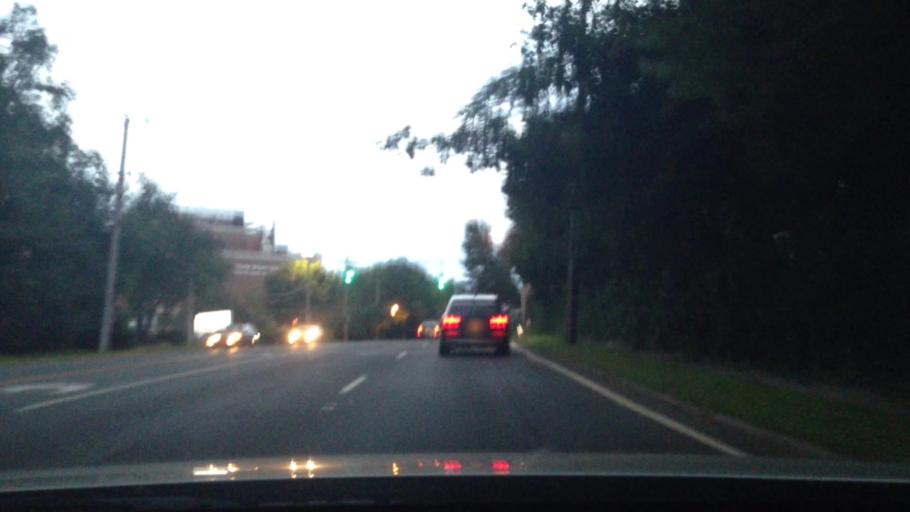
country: US
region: New York
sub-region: Nassau County
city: Thomaston
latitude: 40.7795
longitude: -73.7032
